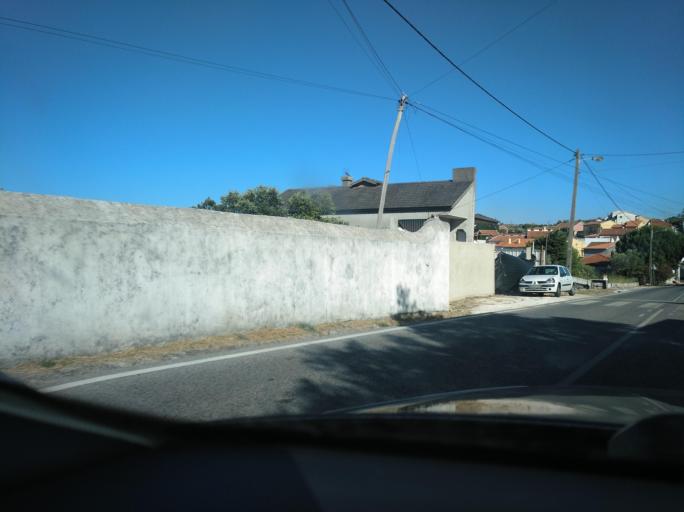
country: PT
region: Santarem
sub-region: Alcanena
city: Alcanena
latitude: 39.5017
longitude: -8.6735
